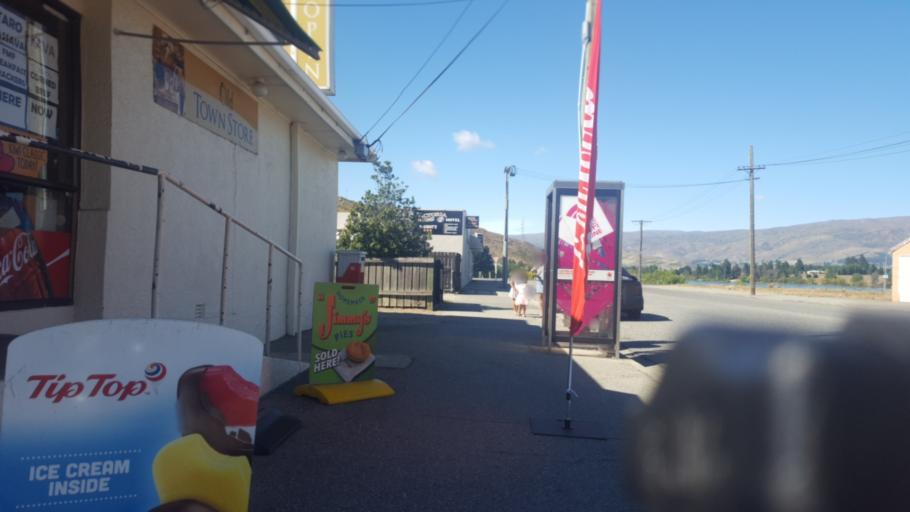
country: NZ
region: Otago
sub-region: Queenstown-Lakes District
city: Wanaka
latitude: -45.0483
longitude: 169.2056
